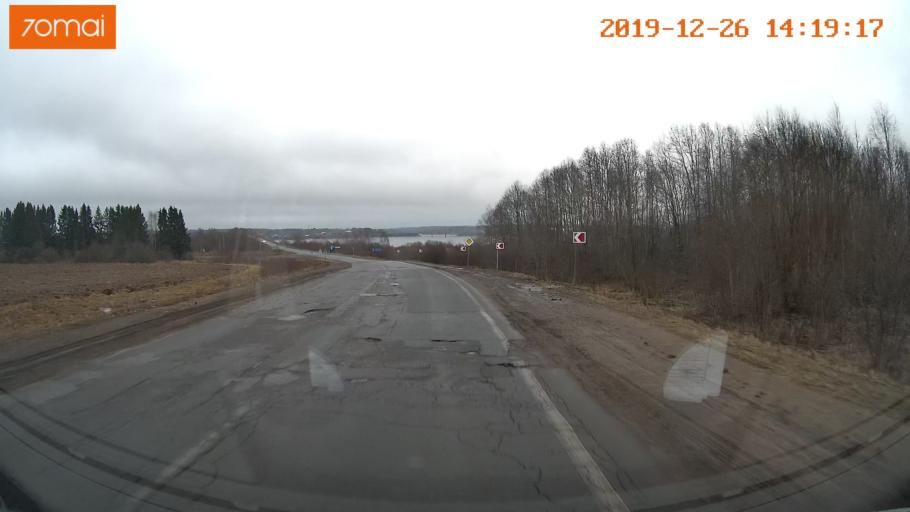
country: RU
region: Jaroslavl
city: Poshekhon'ye
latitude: 58.5109
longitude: 39.1115
